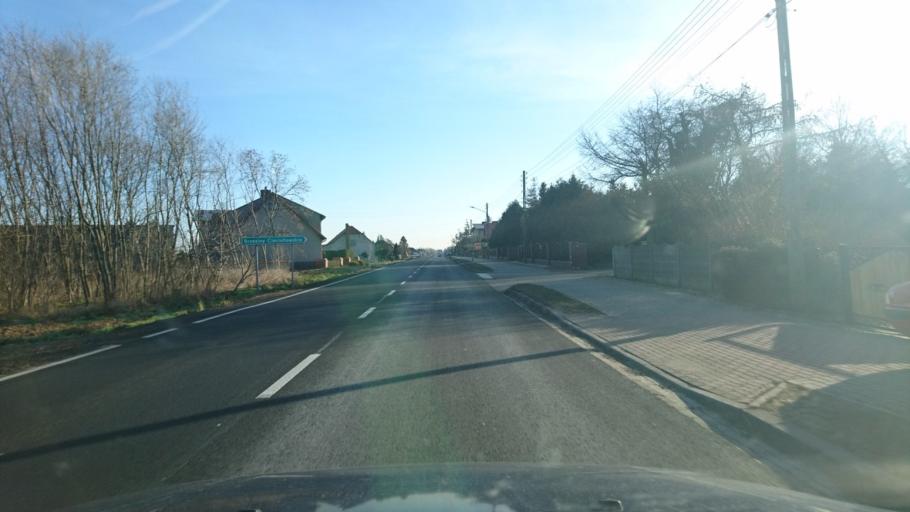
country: PL
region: Silesian Voivodeship
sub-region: Powiat klobucki
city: Starokrzepice
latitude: 51.0029
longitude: 18.6627
